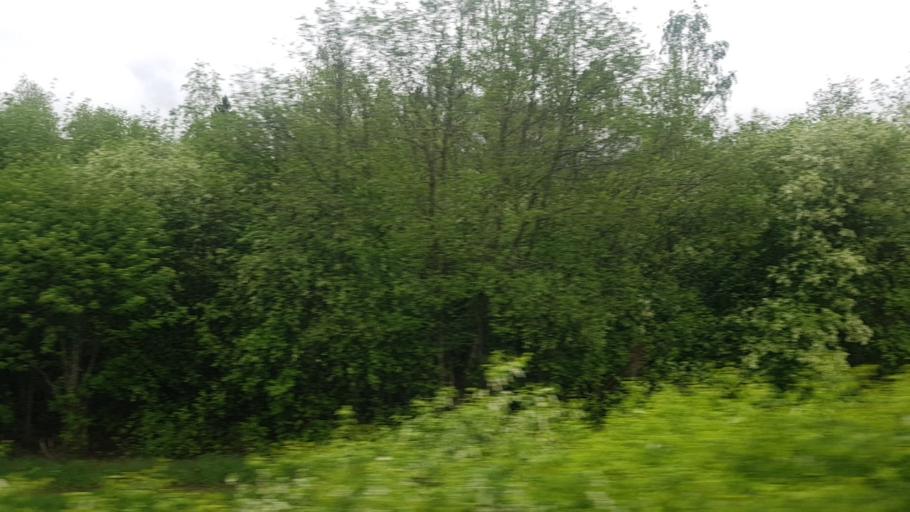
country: NO
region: Oppland
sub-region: Ringebu
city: Ringebu
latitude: 61.4384
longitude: 10.2072
